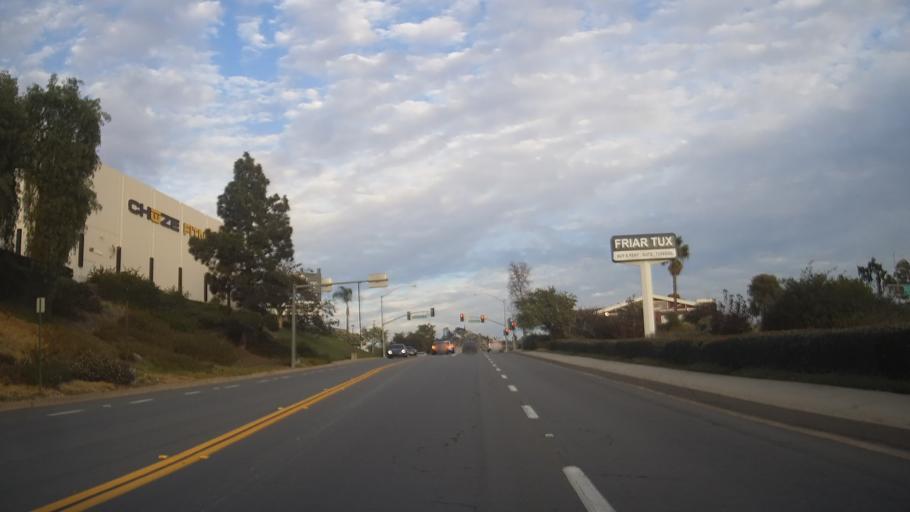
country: US
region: California
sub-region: San Diego County
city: La Mesa
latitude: 32.7763
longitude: -117.0120
